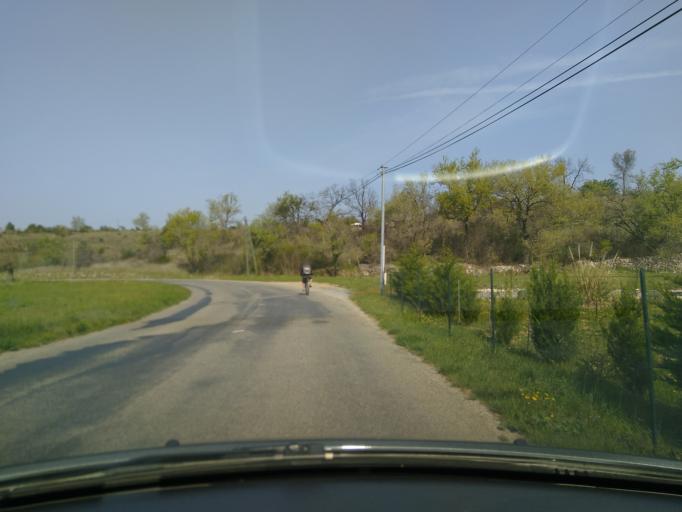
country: FR
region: Rhone-Alpes
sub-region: Departement de l'Ardeche
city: Ruoms
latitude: 44.4496
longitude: 4.3547
